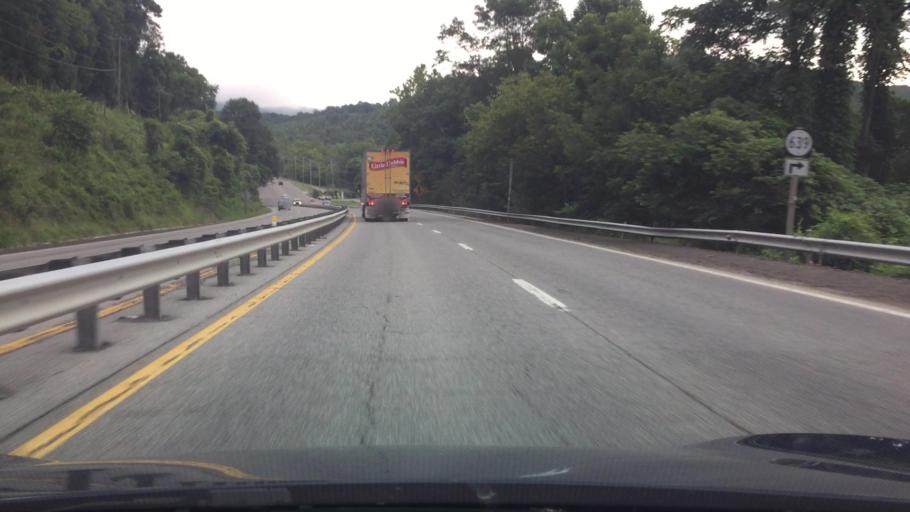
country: US
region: Virginia
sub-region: Montgomery County
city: Shawsville
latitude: 37.2439
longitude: -80.1775
